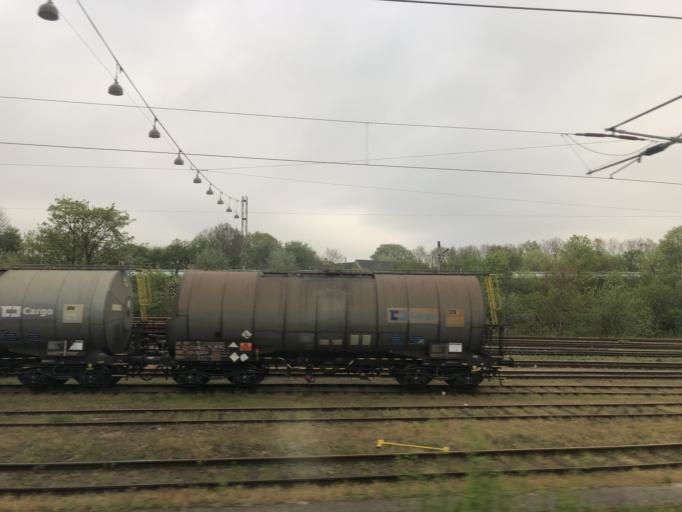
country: DK
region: South Denmark
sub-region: Fredericia Kommune
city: Fredericia
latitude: 55.5802
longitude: 9.7326
